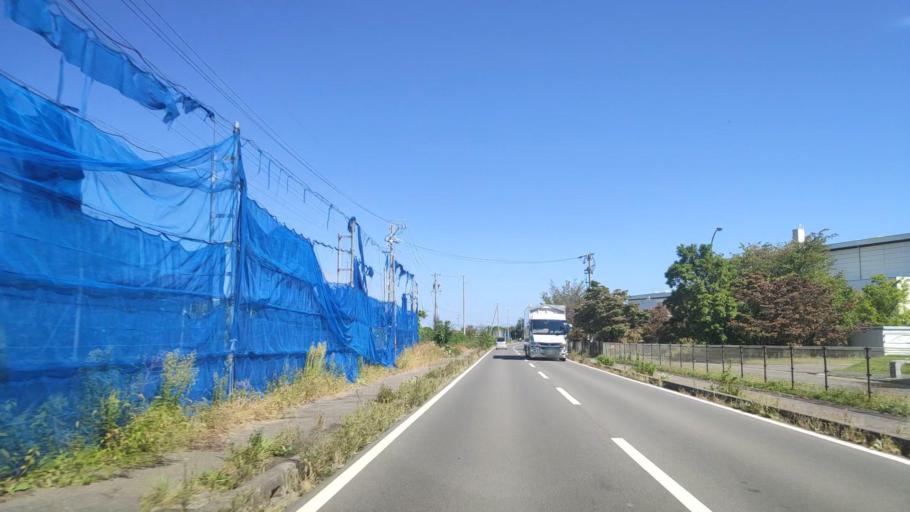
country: JP
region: Nagano
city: Shiojiri
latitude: 36.1643
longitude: 137.9176
